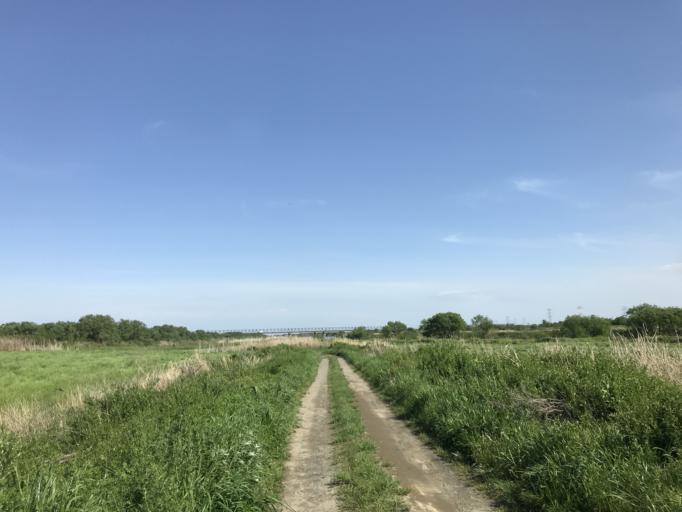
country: JP
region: Ibaraki
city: Moriya
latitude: 35.9401
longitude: 139.9462
